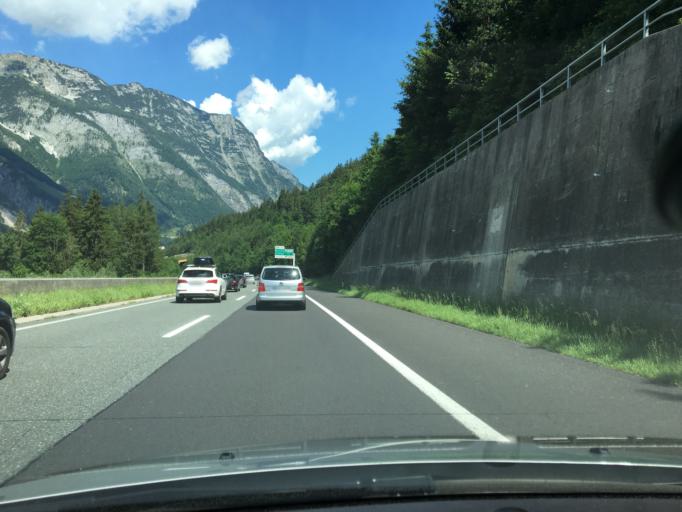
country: AT
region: Salzburg
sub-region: Politischer Bezirk Sankt Johann im Pongau
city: Werfen
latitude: 47.5011
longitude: 13.1793
